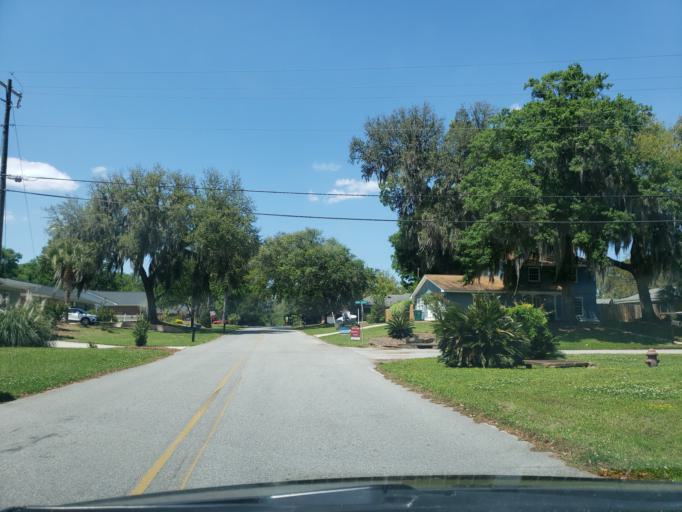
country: US
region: Georgia
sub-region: Chatham County
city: Whitemarsh Island
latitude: 32.0517
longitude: -81.0164
